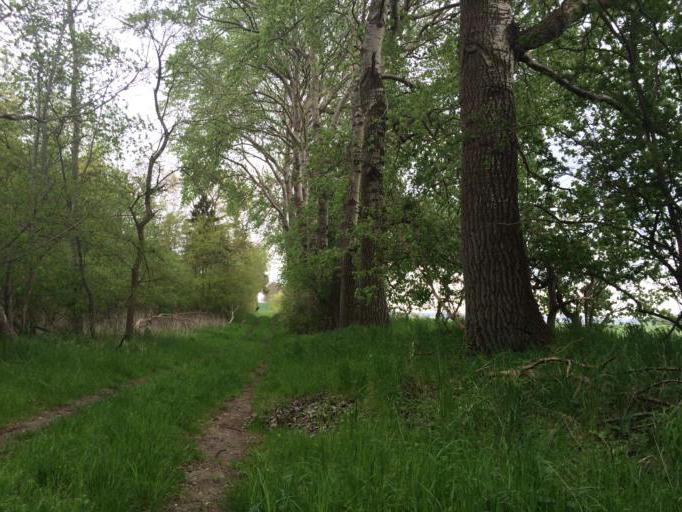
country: DK
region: Zealand
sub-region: Lejre Kommune
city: Ejby
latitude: 55.7599
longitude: 11.8170
